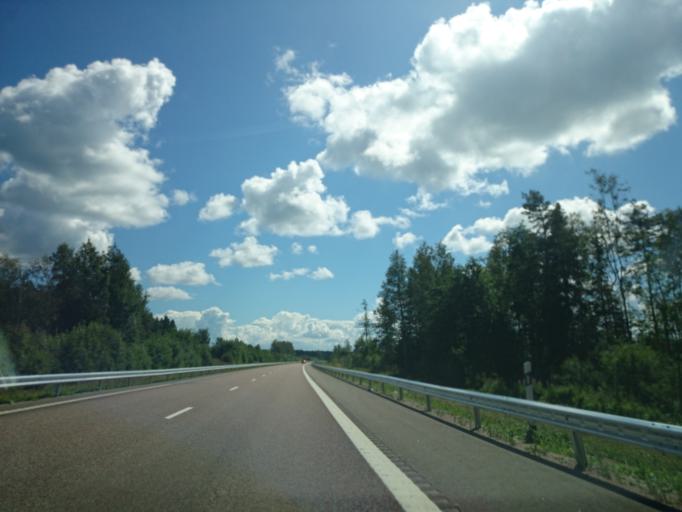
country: SE
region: Gaevleborg
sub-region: Gavle Kommun
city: Gavle
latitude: 60.5797
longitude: 17.2160
